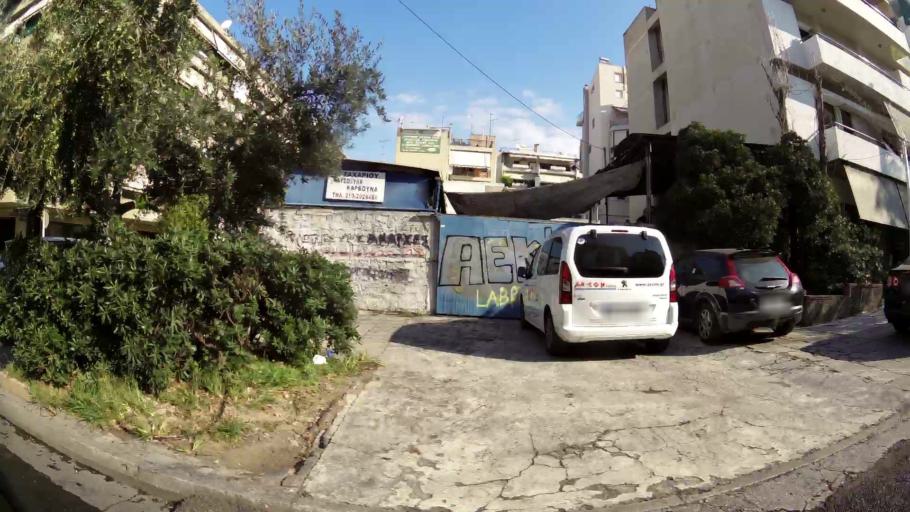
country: GR
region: Attica
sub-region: Nomarchia Athinas
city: Galatsi
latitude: 38.0205
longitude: 23.7453
